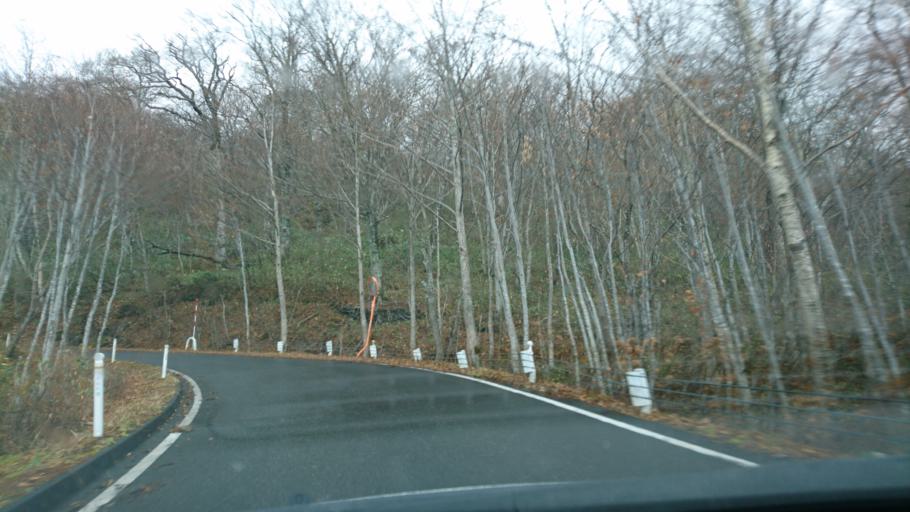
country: JP
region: Iwate
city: Ichinoseki
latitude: 38.9430
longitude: 140.8161
